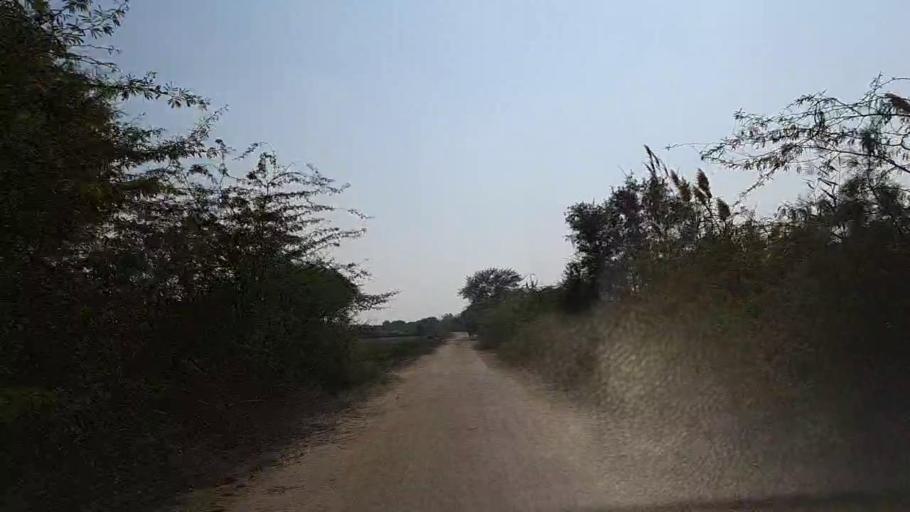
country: PK
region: Sindh
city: Jam Sahib
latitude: 26.2636
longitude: 68.5286
